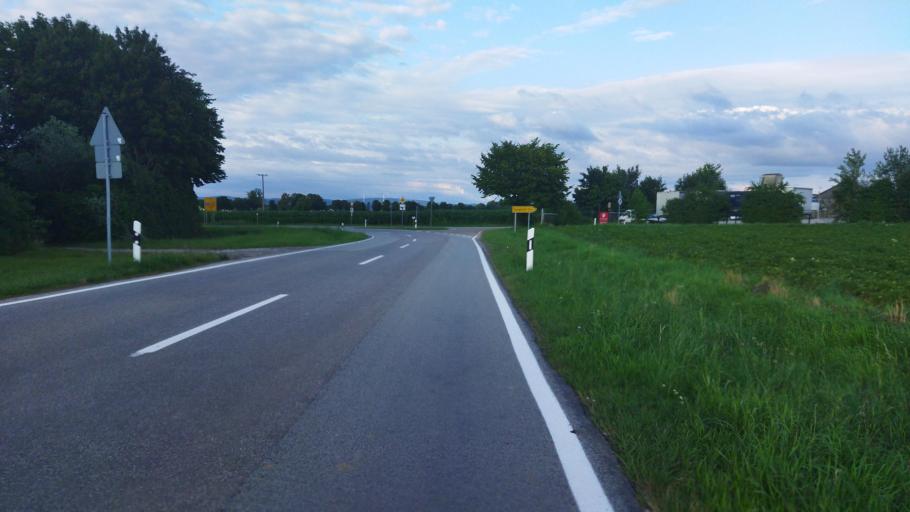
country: DE
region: Bavaria
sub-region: Upper Palatinate
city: Riekofen
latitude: 48.9653
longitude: 12.3249
